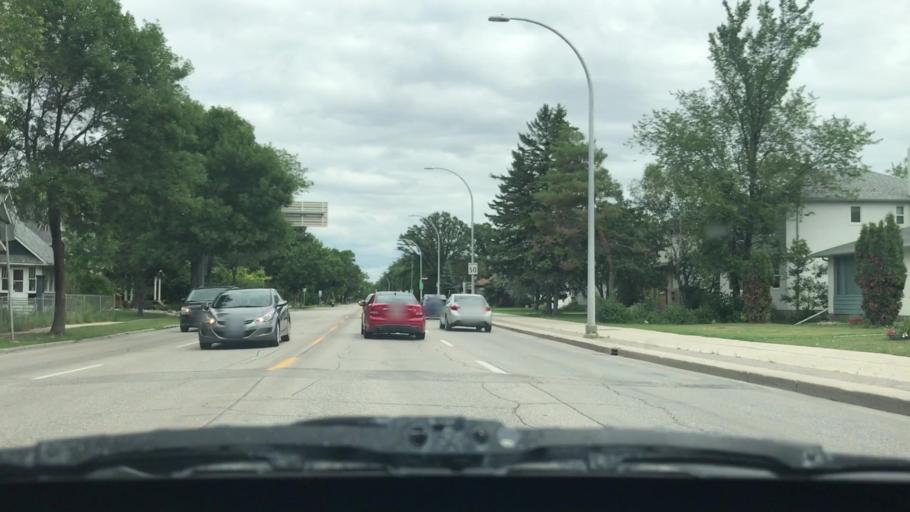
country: CA
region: Manitoba
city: Winnipeg
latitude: 49.8536
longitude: -97.1482
